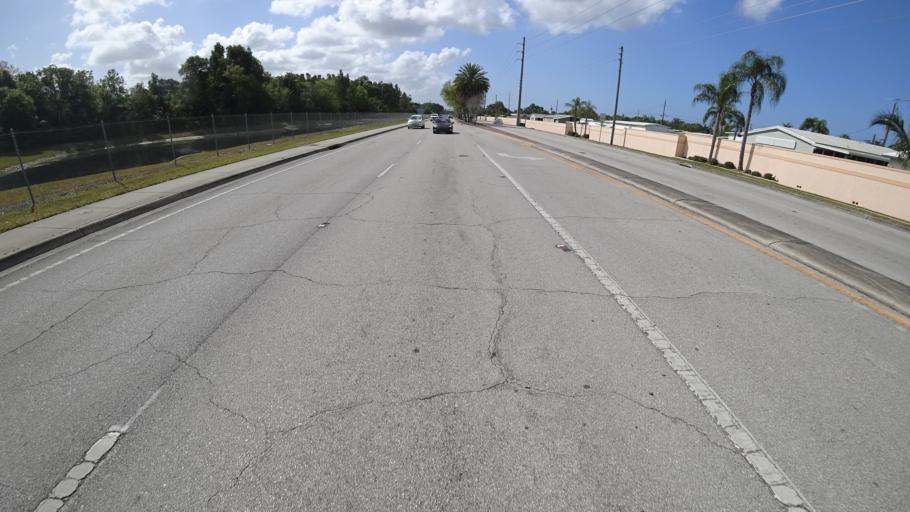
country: US
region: Florida
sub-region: Manatee County
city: West Samoset
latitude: 27.4504
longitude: -82.5549
